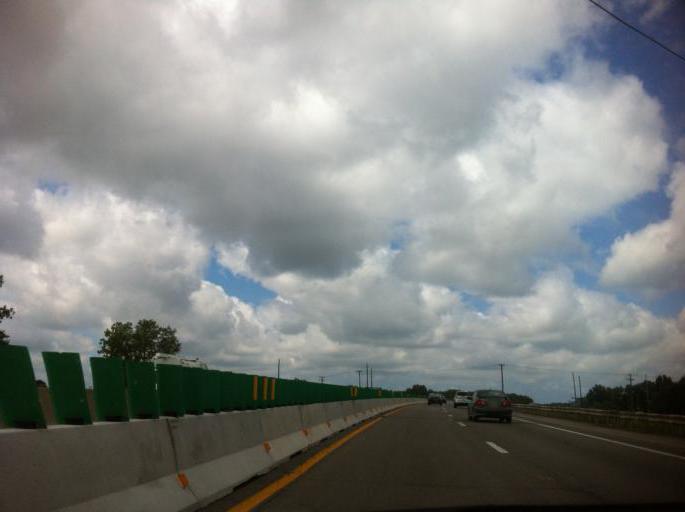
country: US
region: Ohio
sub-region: Lorain County
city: Elyria
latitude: 41.3795
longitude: -82.0643
